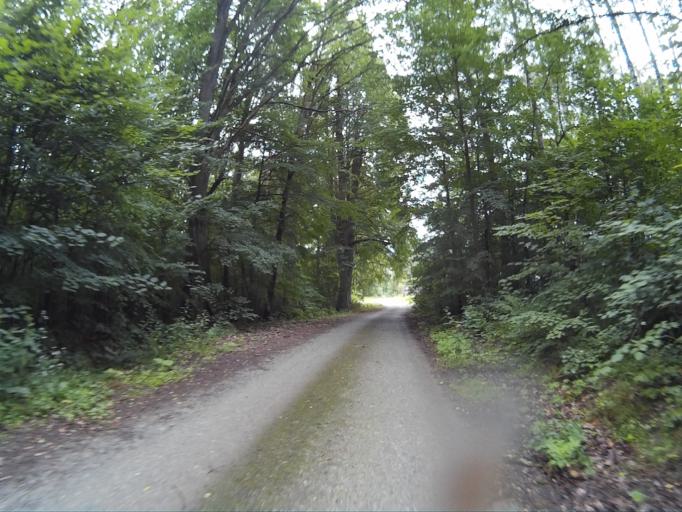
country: PL
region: Kujawsko-Pomorskie
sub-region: Powiat swiecki
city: Lniano
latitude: 53.6108
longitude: 18.2010
